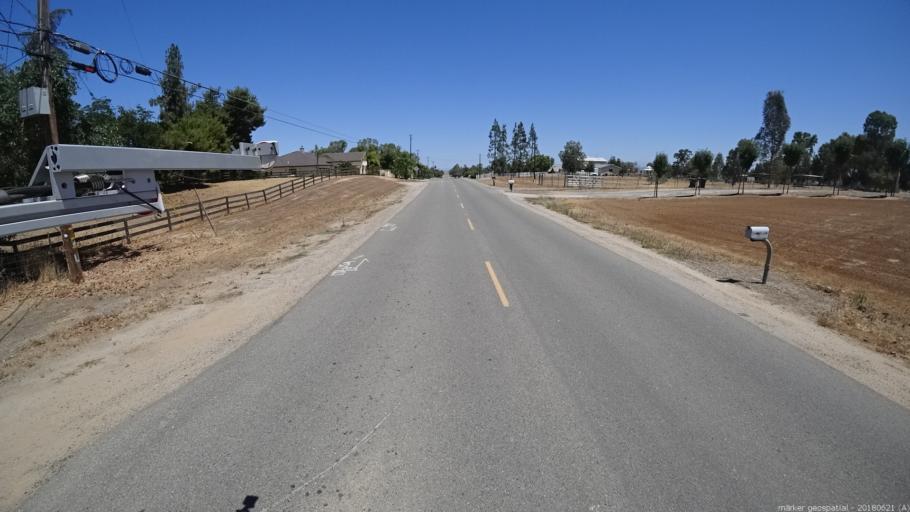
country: US
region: California
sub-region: Madera County
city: Bonadelle Ranchos-Madera Ranchos
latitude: 36.9967
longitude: -119.8757
